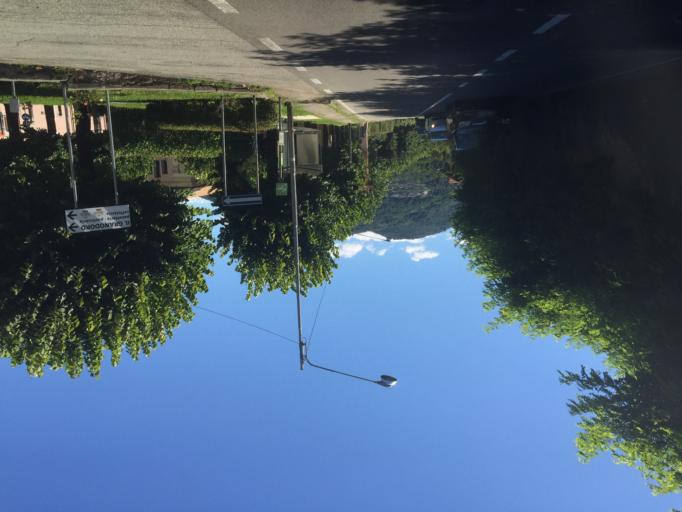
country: IT
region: Lombardy
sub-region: Provincia di Varese
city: Lavena Ponte Tresa
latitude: 45.9577
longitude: 8.8690
